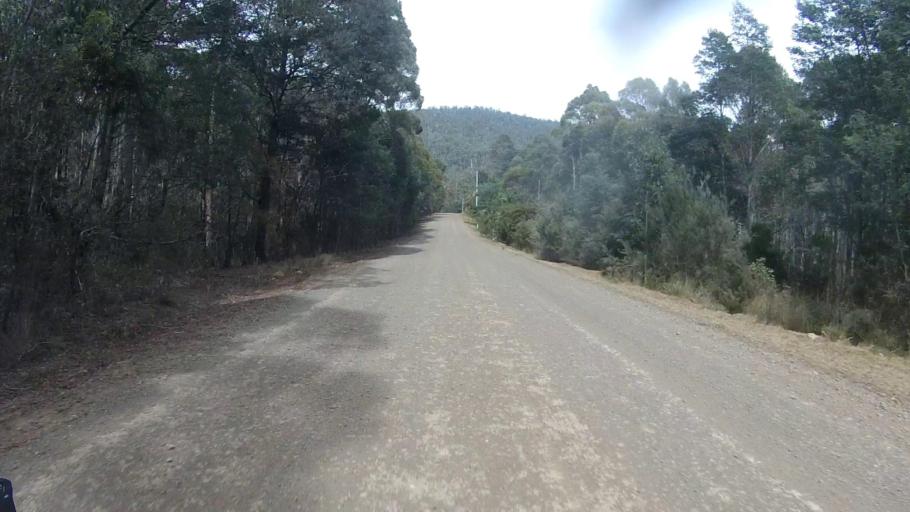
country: AU
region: Tasmania
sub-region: Sorell
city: Sorell
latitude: -42.6888
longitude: 147.8694
